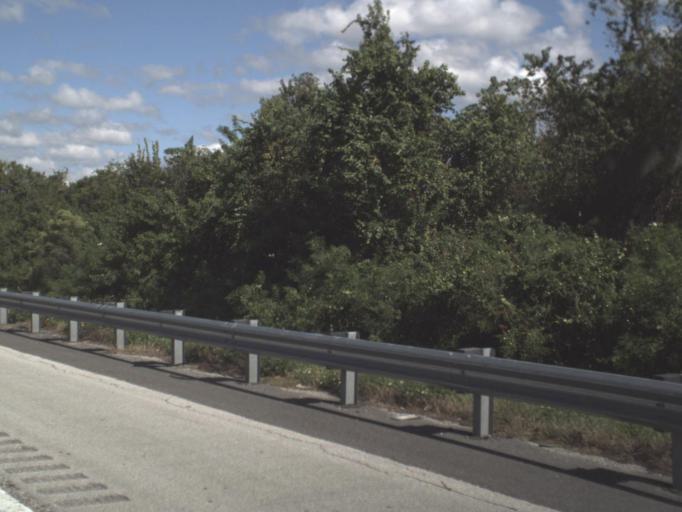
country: US
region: Florida
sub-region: Osceola County
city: Saint Cloud
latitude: 28.2413
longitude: -81.3264
